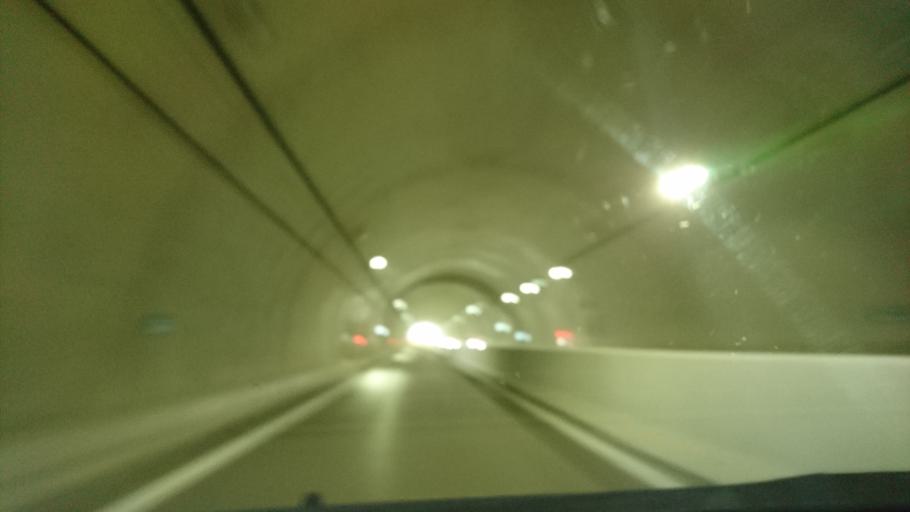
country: JP
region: Iwate
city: Ofunato
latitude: 38.9696
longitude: 141.6241
